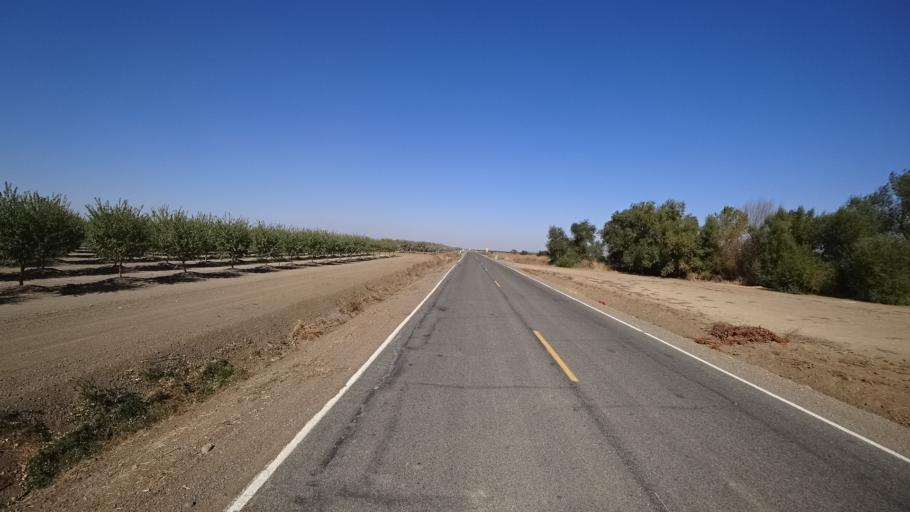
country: US
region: California
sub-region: Yolo County
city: Winters
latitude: 38.5873
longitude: -121.9050
